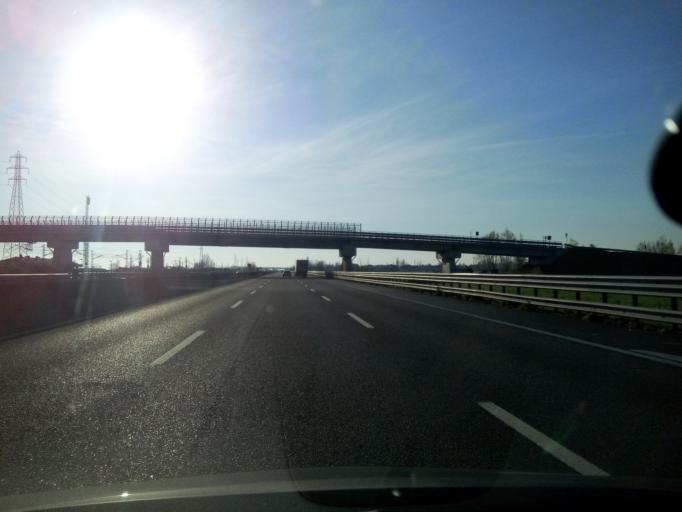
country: IT
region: Emilia-Romagna
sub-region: Provincia di Parma
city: San Prospero
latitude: 44.8164
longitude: 10.4067
